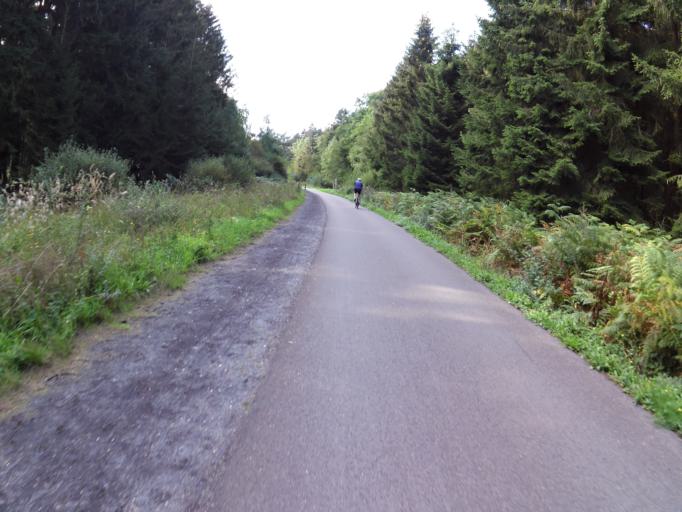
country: BE
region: Wallonia
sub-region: Province de Liege
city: Raeren
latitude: 50.6592
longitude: 6.1382
